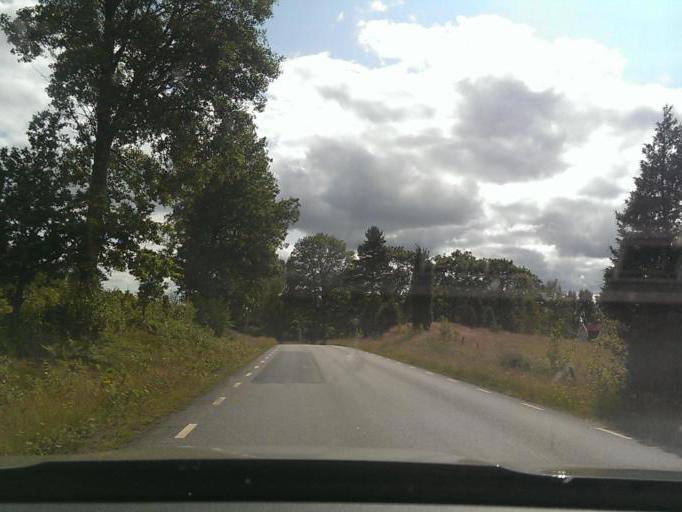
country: SE
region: Joenkoeping
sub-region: Varnamo Kommun
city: Forsheda
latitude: 57.0811
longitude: 13.8725
